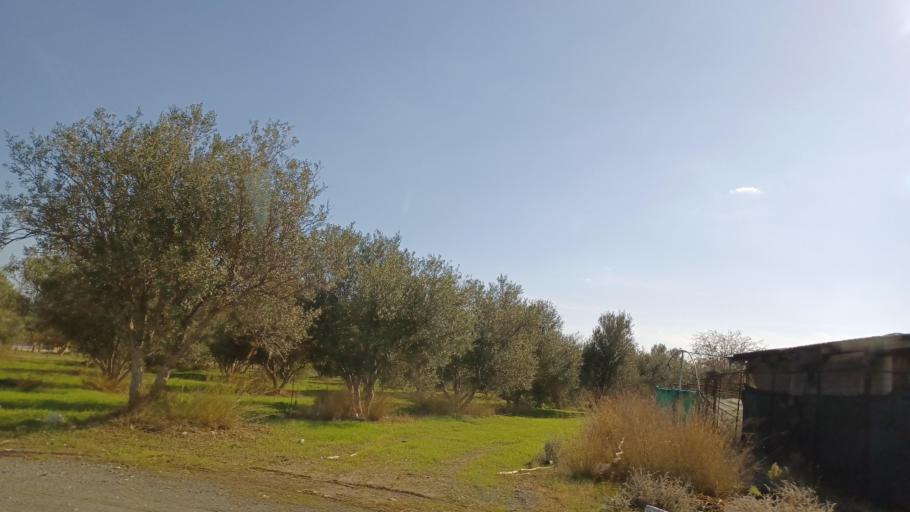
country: CY
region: Larnaka
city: Kofinou
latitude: 34.7545
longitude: 33.3178
